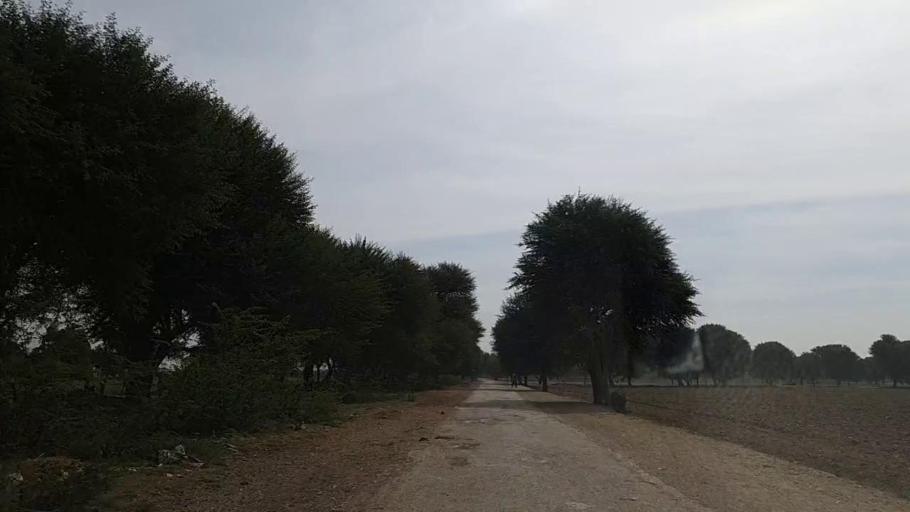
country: PK
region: Sindh
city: Samaro
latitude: 25.2859
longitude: 69.4196
